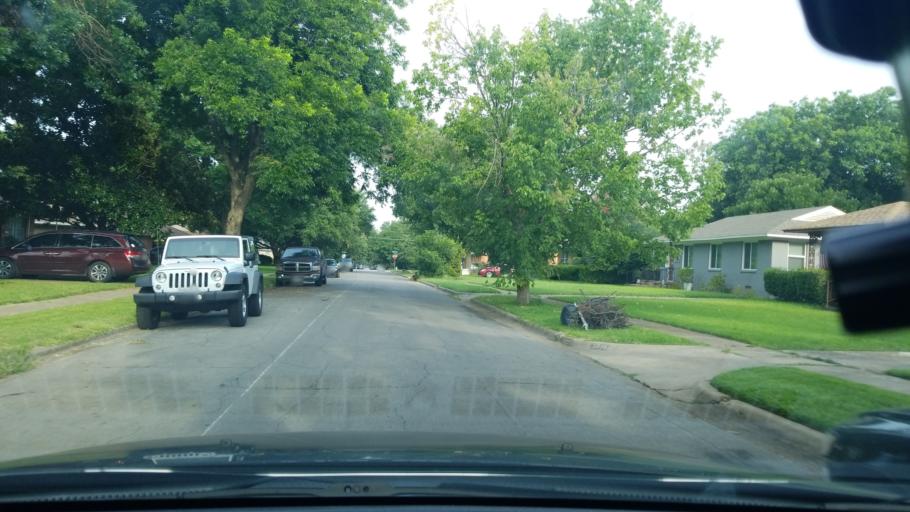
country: US
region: Texas
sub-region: Dallas County
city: Garland
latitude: 32.8312
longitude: -96.6667
